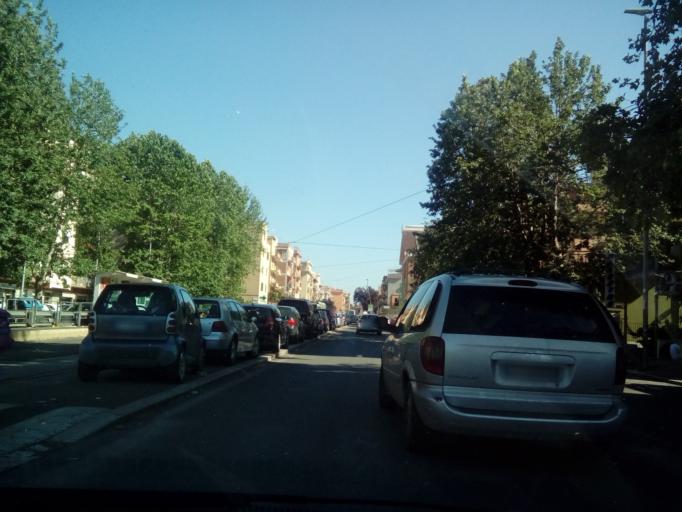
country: IT
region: Latium
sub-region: Citta metropolitana di Roma Capitale
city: Rome
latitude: 41.8912
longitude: 12.5642
